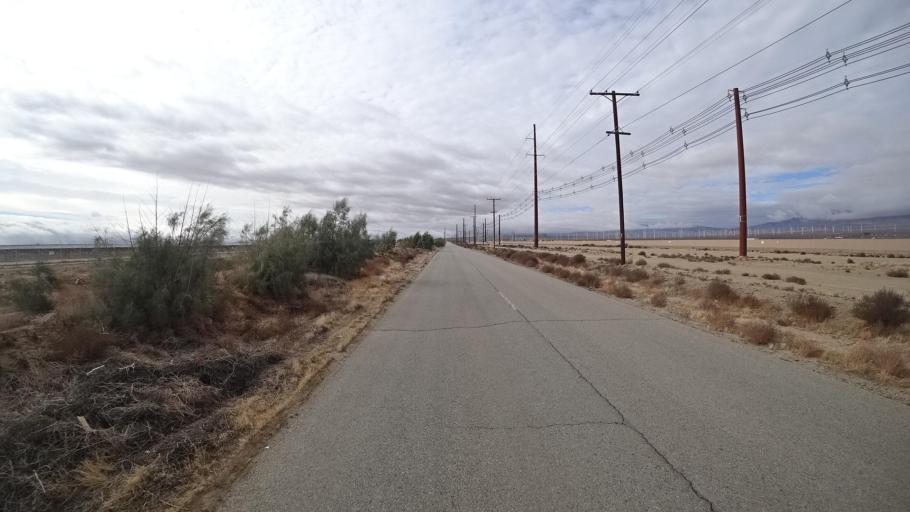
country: US
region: California
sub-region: Kern County
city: Rosamond
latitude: 34.8636
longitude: -118.3708
